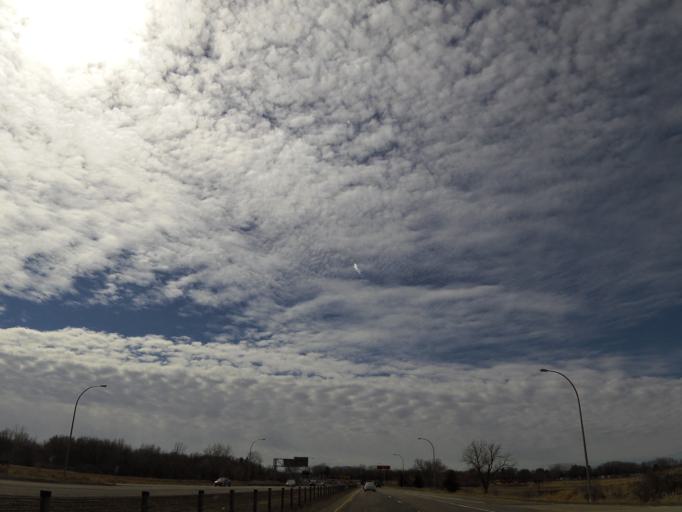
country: US
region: Minnesota
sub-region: Ramsey County
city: North Saint Paul
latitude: 45.0289
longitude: -92.9659
